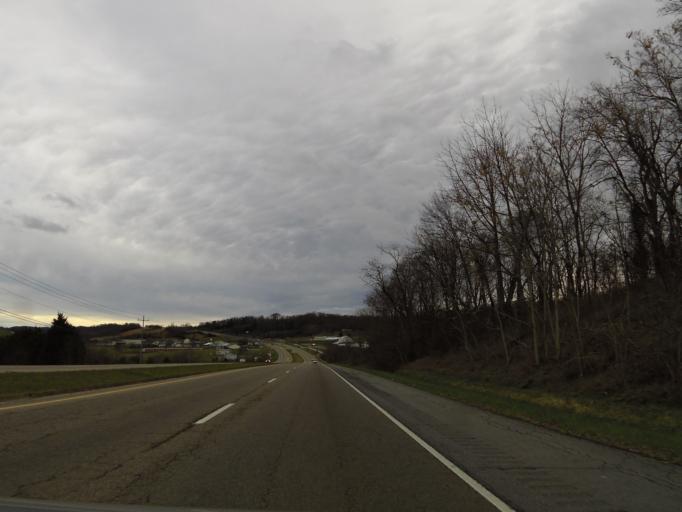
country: US
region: Tennessee
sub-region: Washington County
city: Jonesborough
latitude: 36.2611
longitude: -82.5564
